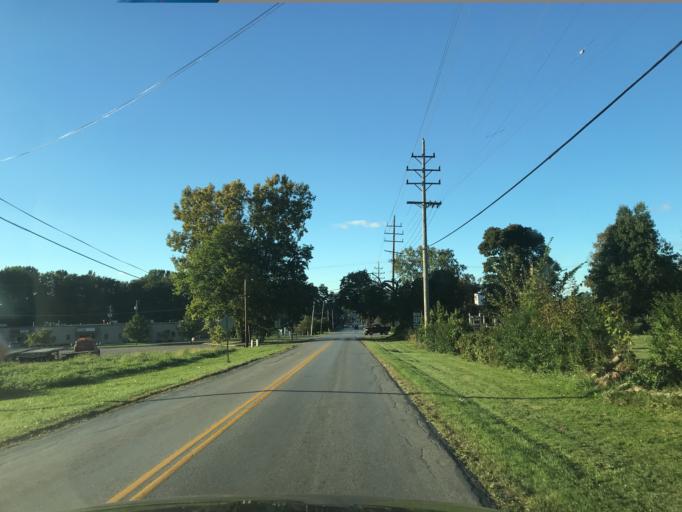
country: US
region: Ohio
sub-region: Ashtabula County
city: Edgewood
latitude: 41.8597
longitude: -80.7695
